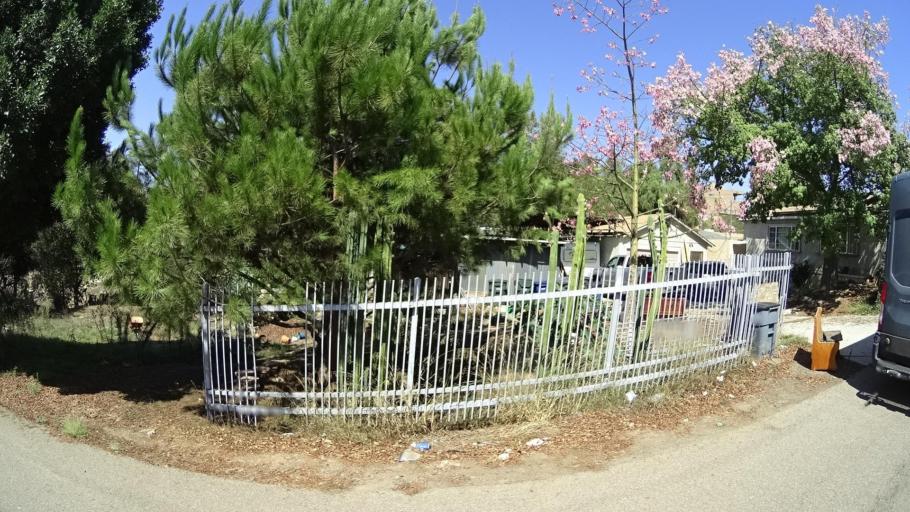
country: US
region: California
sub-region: San Diego County
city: Crest
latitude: 32.8107
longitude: -116.8667
